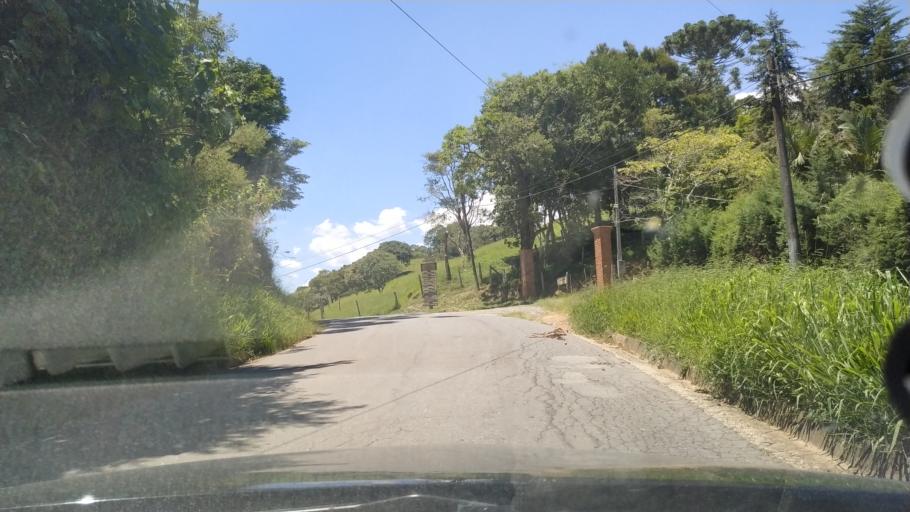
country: BR
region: Sao Paulo
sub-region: Campos Do Jordao
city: Campos do Jordao
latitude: -22.8175
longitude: -45.6805
